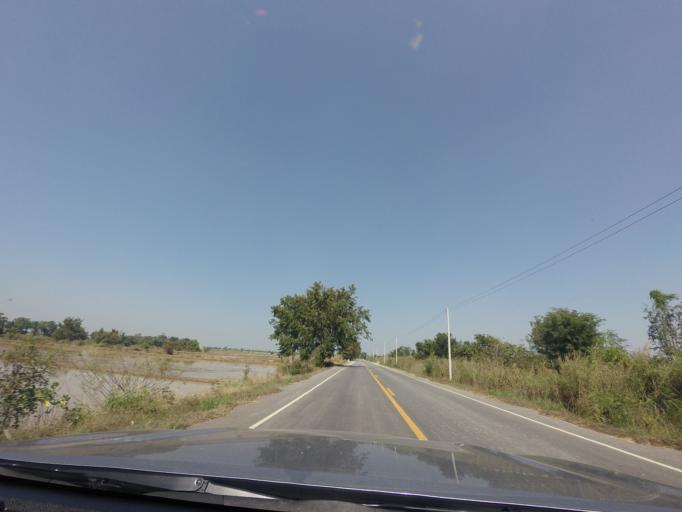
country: TH
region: Sukhothai
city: Sukhothai
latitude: 17.0818
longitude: 99.7907
